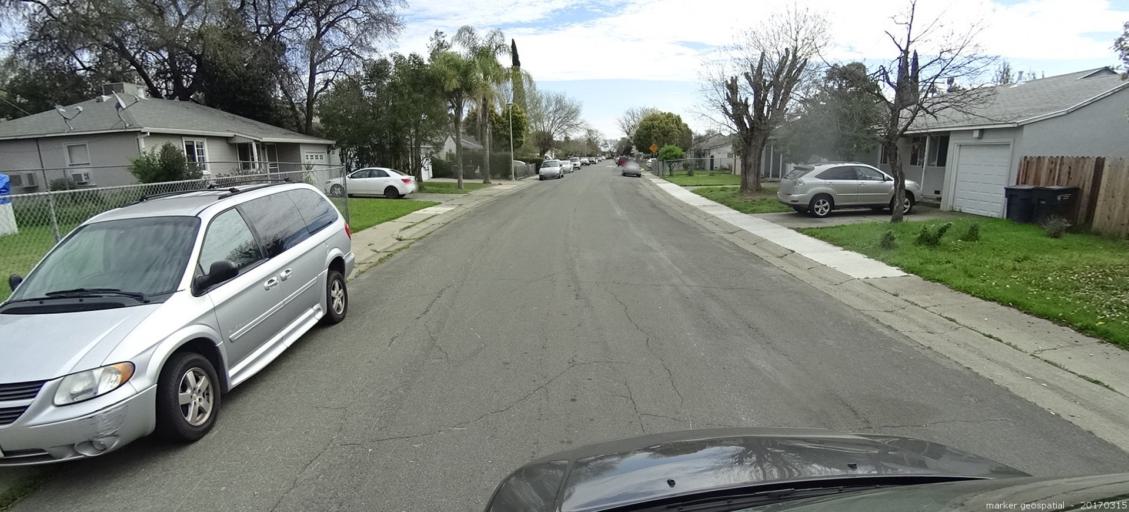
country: US
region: California
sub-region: Sacramento County
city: Parkway
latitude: 38.5210
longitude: -121.5046
